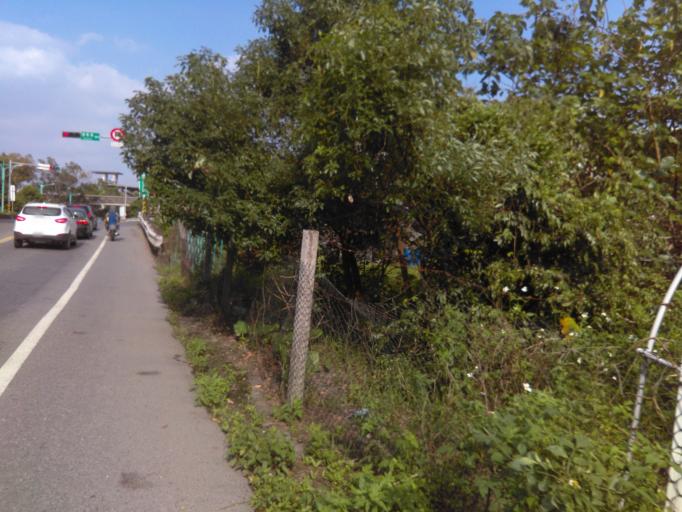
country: TW
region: Taiwan
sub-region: Yilan
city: Yilan
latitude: 24.7608
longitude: 121.7486
